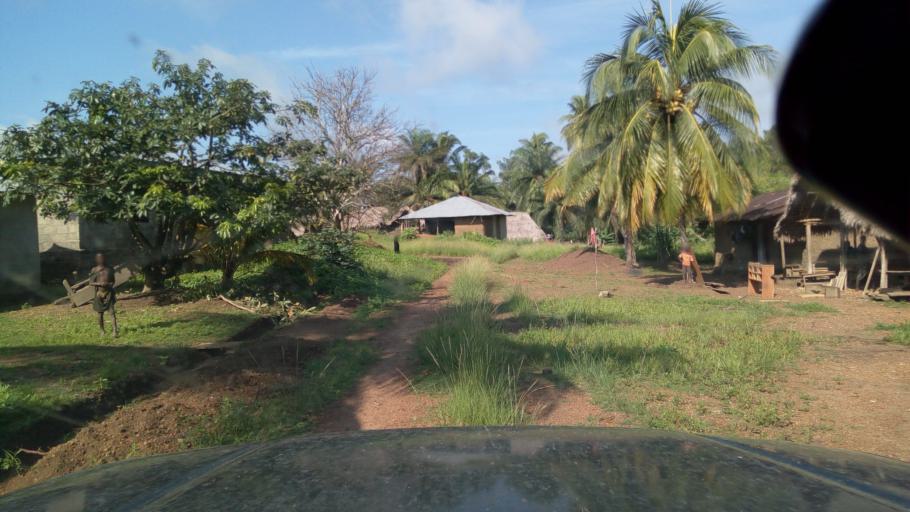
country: SL
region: Southern Province
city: Koribundu
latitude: 7.7010
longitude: -11.5285
